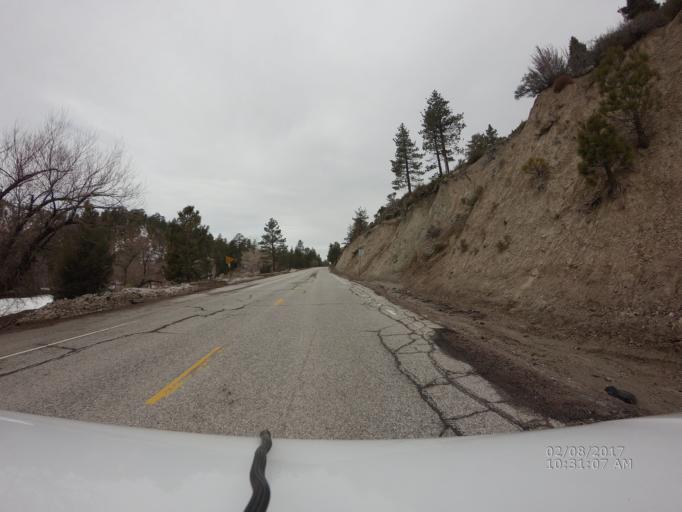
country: US
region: California
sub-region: San Bernardino County
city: Pinon Hills
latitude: 34.3926
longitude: -117.7258
